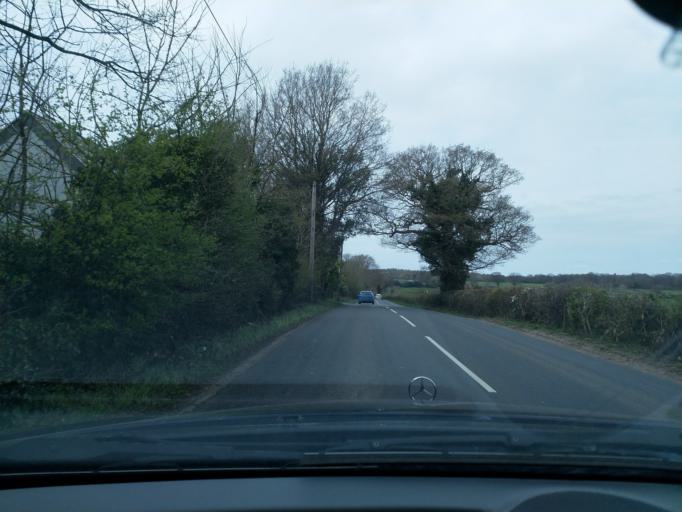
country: GB
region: England
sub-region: Warwickshire
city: Royal Leamington Spa
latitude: 52.3240
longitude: -1.5469
